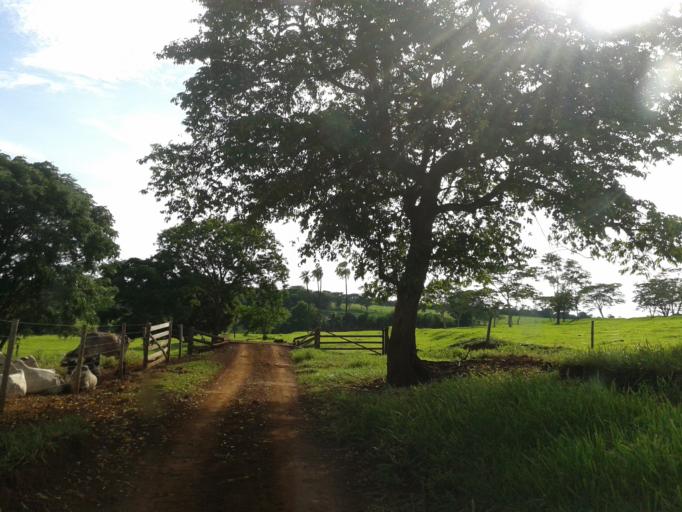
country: BR
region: Minas Gerais
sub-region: Centralina
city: Centralina
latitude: -18.7096
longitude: -49.1919
